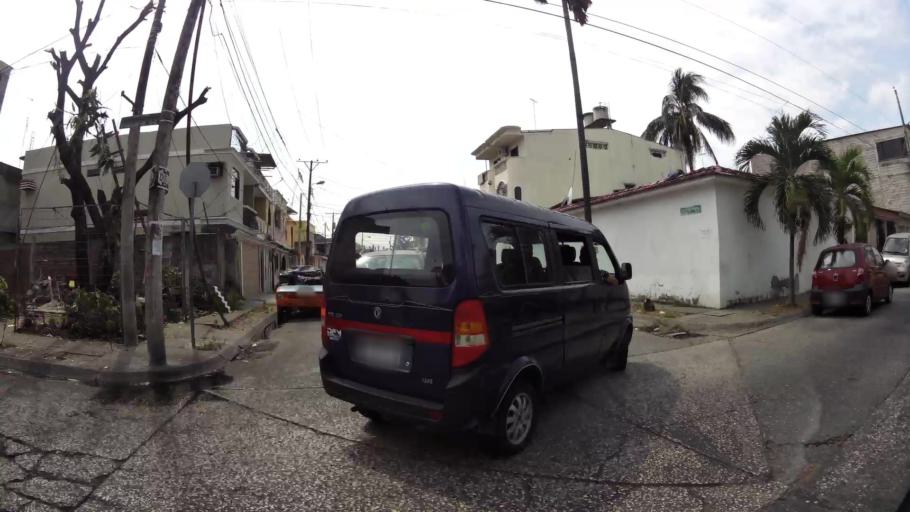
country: EC
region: Guayas
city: Eloy Alfaro
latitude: -2.1235
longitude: -79.8981
